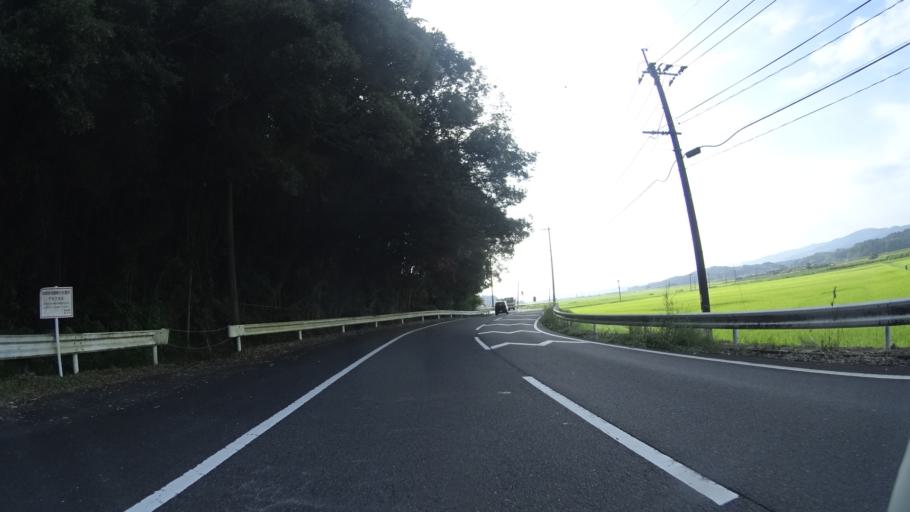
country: JP
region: Kagoshima
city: Okuchi-shinohara
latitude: 32.0233
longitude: 130.6099
